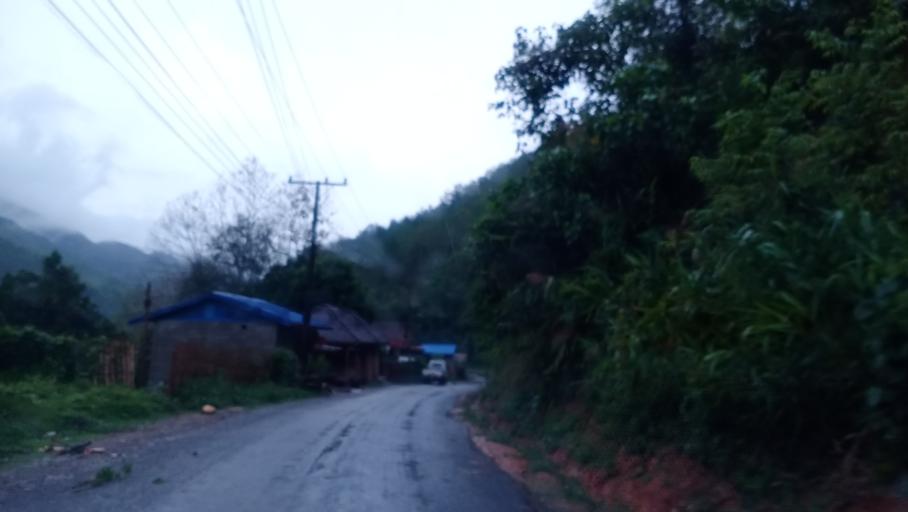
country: LA
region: Phongsali
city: Khoa
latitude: 21.0703
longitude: 102.4923
